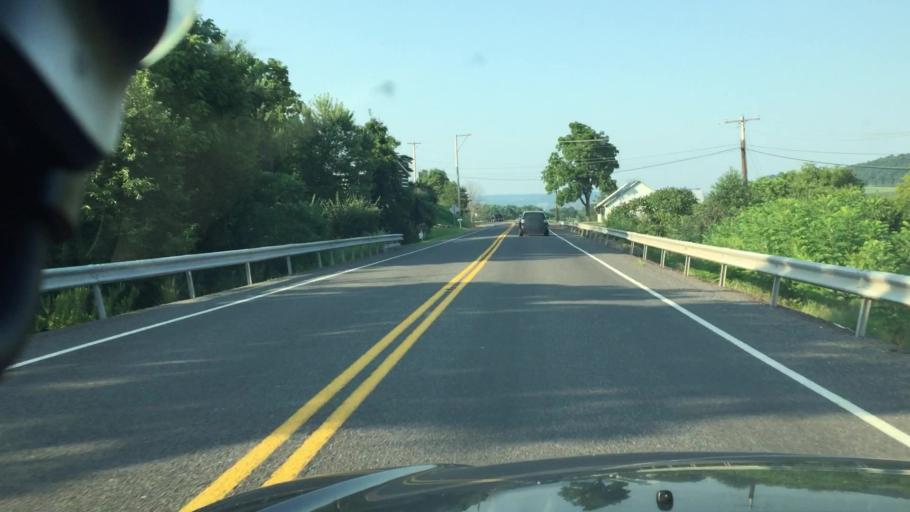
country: US
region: Pennsylvania
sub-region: Columbia County
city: Mifflinville
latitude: 41.0057
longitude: -76.3212
